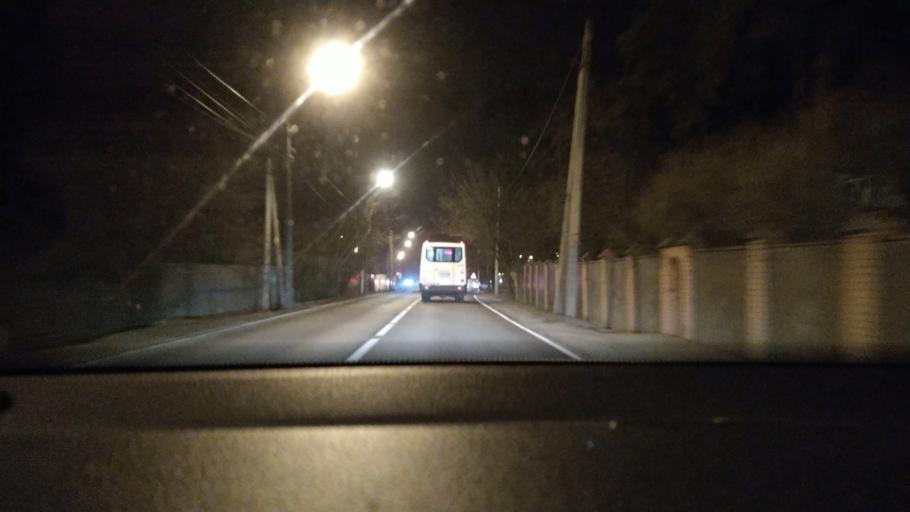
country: RU
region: Moskovskaya
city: Selyatino
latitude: 55.4719
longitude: 36.9277
